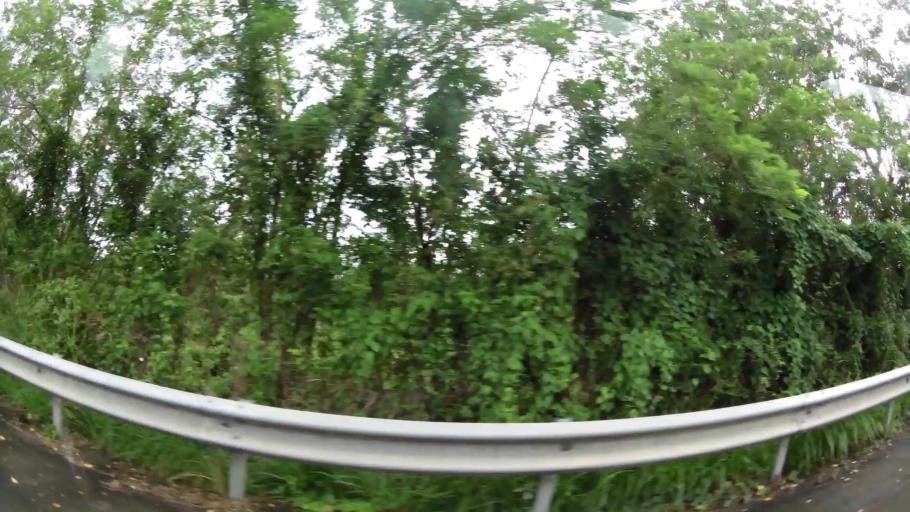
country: MQ
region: Martinique
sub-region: Martinique
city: Les Trois-Ilets
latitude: 14.5059
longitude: -60.9817
